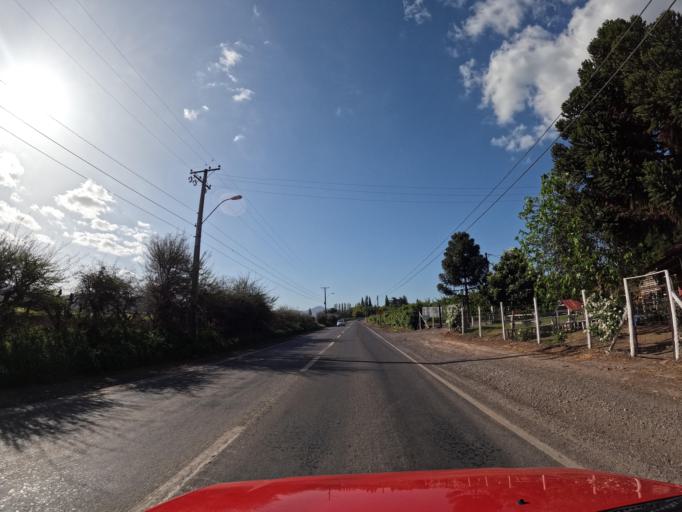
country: CL
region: Maule
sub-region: Provincia de Curico
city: Rauco
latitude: -34.9090
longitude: -71.2786
